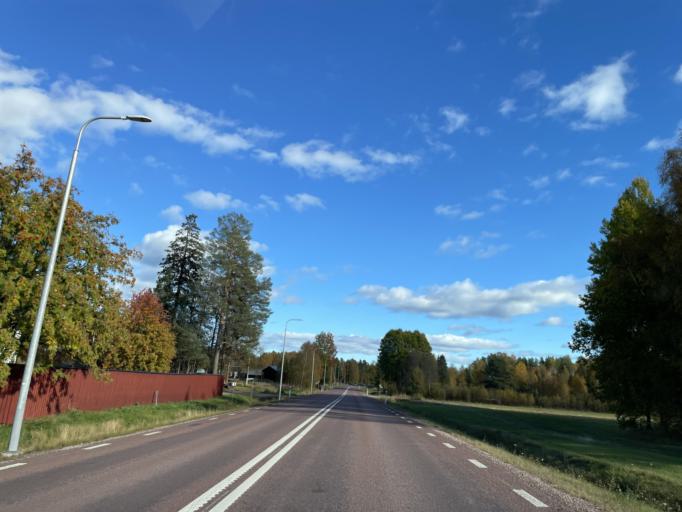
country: SE
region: Dalarna
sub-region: Malung-Saelens kommun
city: Malung
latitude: 60.7123
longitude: 13.6268
